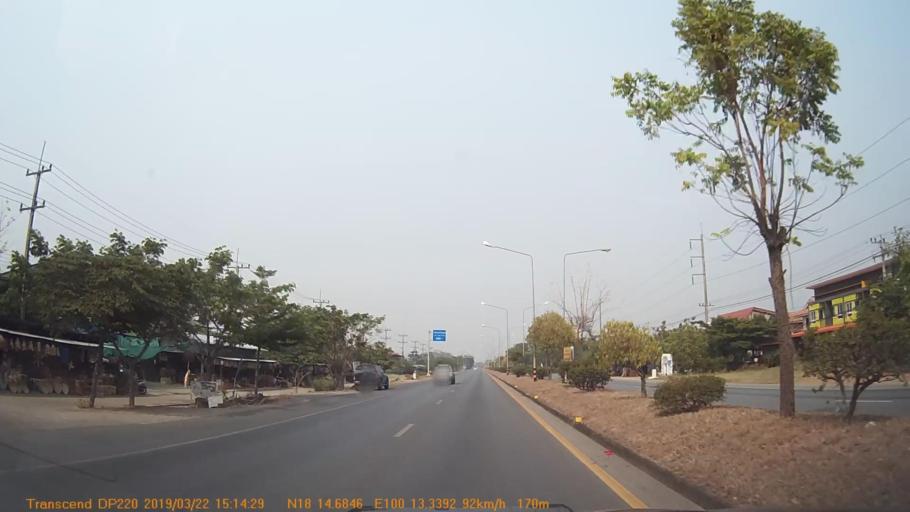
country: TH
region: Phrae
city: Nong Muang Khai
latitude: 18.2451
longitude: 100.2226
